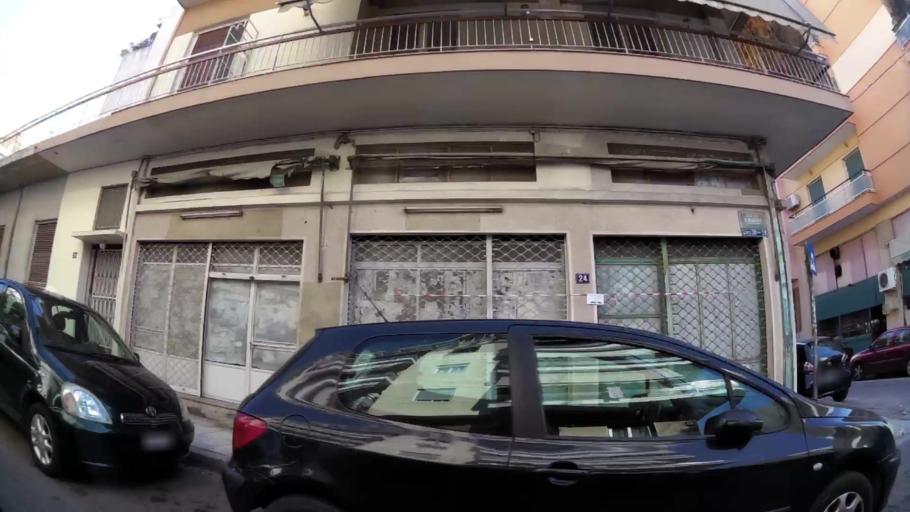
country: GR
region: Attica
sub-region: Nomarchia Athinas
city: Tavros
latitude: 37.9681
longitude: 23.7047
